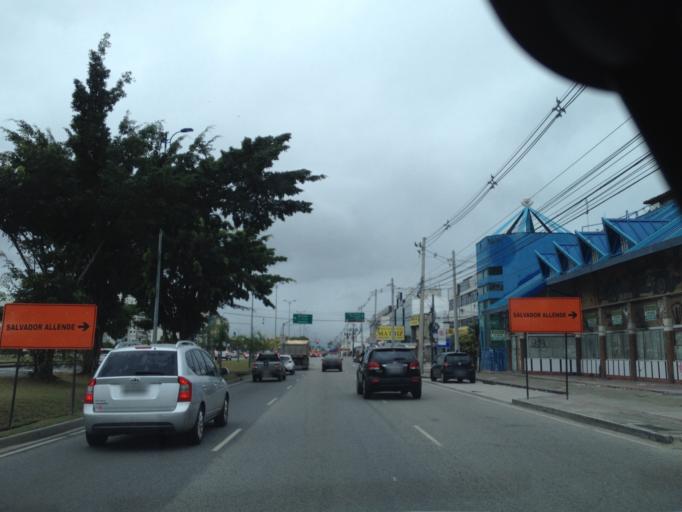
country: BR
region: Rio de Janeiro
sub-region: Nilopolis
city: Nilopolis
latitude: -23.0096
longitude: -43.4465
